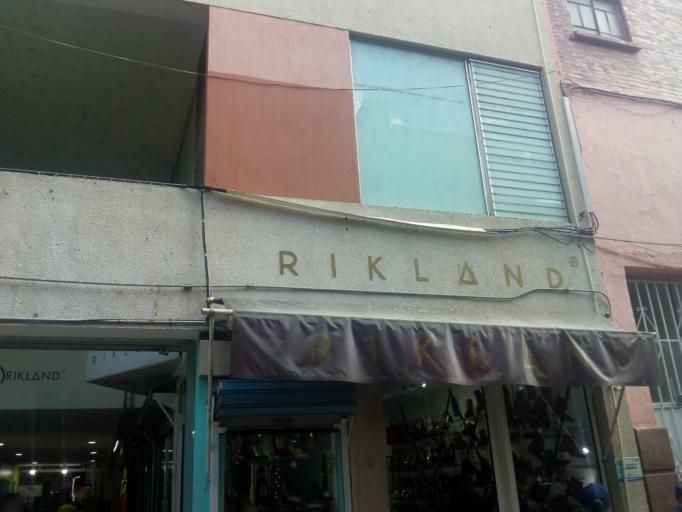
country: MX
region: Guanajuato
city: Leon
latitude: 21.1229
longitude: -101.6823
